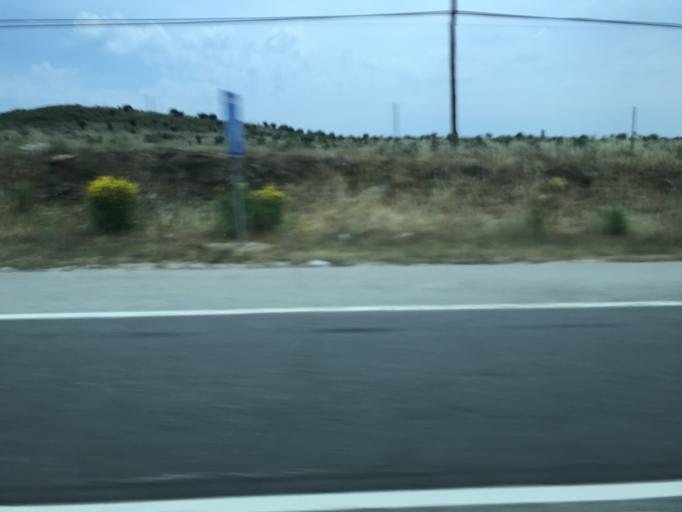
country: ES
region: Madrid
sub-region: Provincia de Madrid
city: Gascones
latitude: 41.0133
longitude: -3.6304
